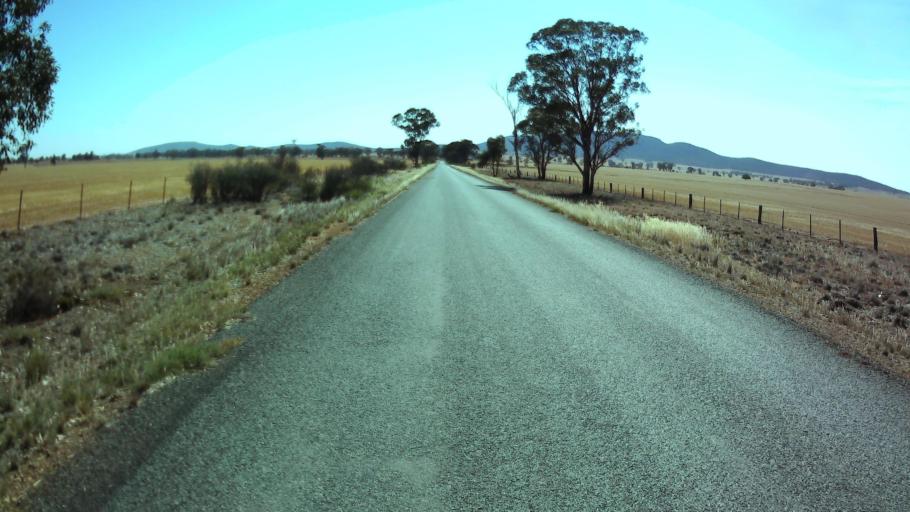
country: AU
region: New South Wales
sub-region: Weddin
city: Grenfell
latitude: -33.7525
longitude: 147.8658
